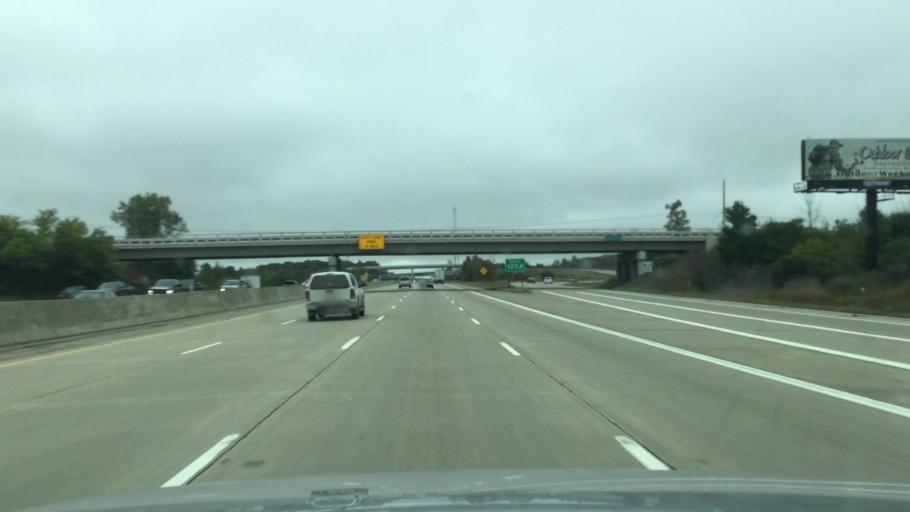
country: US
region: Michigan
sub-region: Genesee County
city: Mount Morris
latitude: 43.1054
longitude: -83.7634
